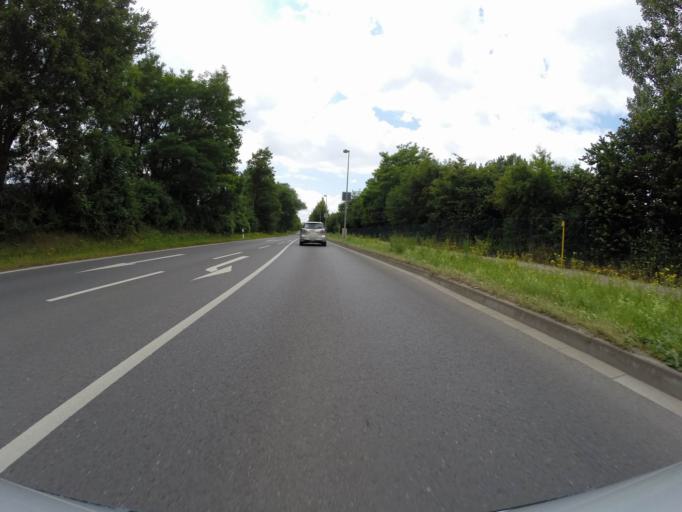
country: DE
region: Thuringia
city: Jena
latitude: 50.9434
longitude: 11.6067
